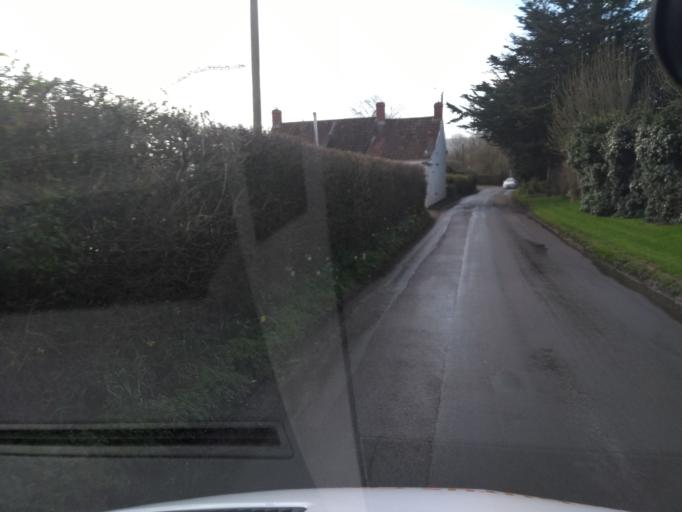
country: GB
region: England
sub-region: Somerset
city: Street
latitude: 51.1274
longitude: -2.8240
